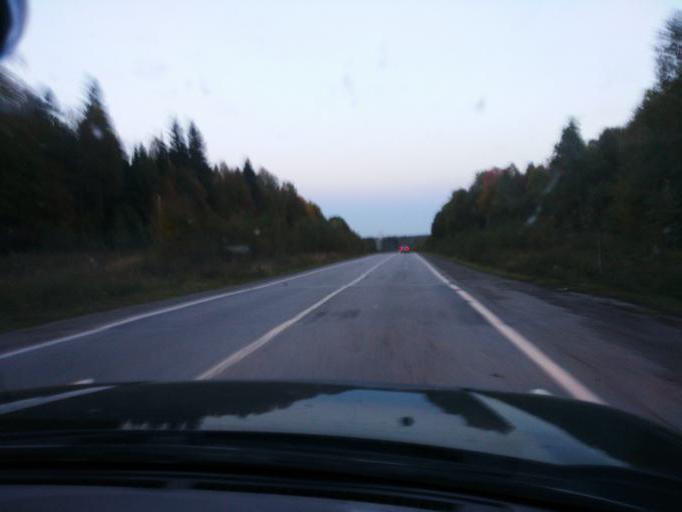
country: RU
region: Perm
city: Verkhnechusovskiye Gorodki
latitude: 58.2606
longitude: 56.9808
